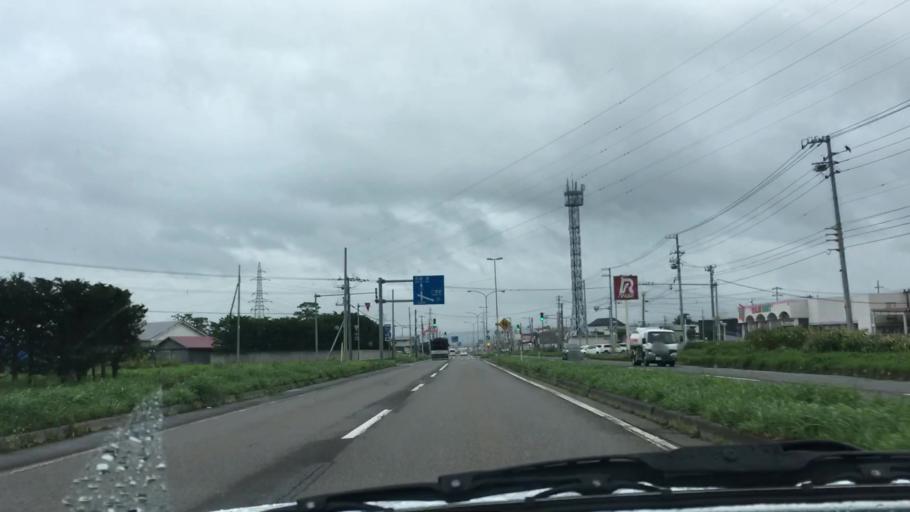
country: JP
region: Hokkaido
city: Nanae
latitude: 42.2595
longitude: 140.2770
